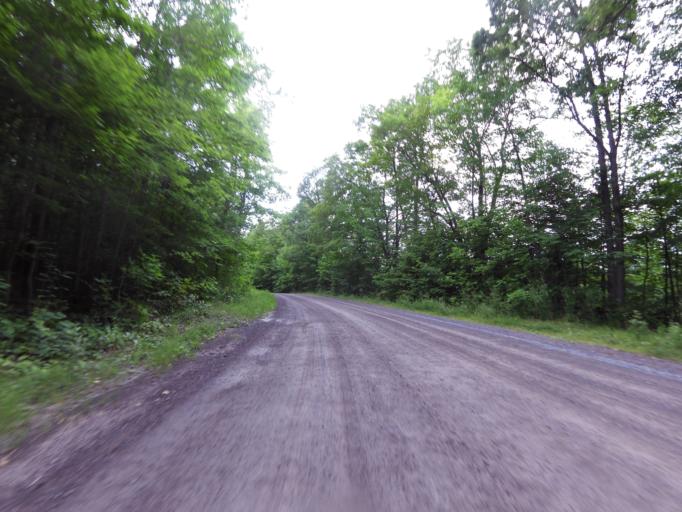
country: CA
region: Ontario
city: Carleton Place
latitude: 45.1487
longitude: -76.2202
